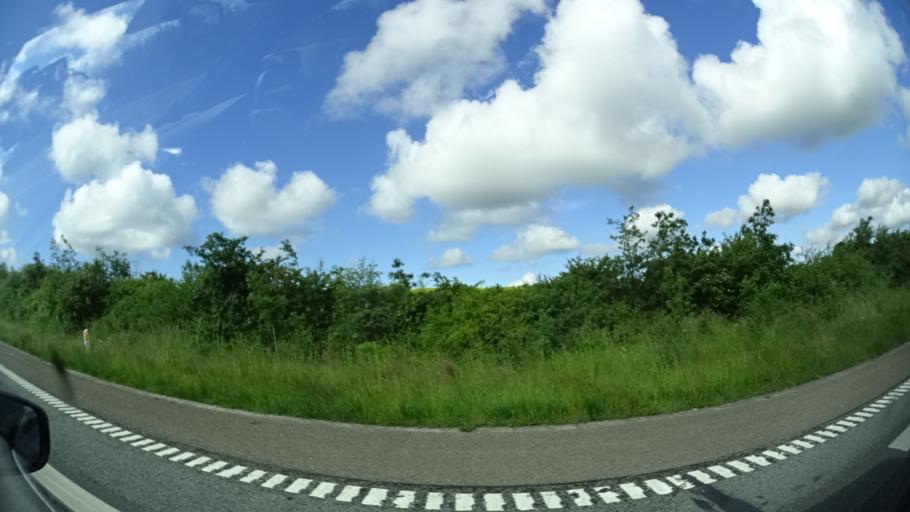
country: DK
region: Central Jutland
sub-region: Syddjurs Kommune
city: Ronde
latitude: 56.3068
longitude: 10.5033
